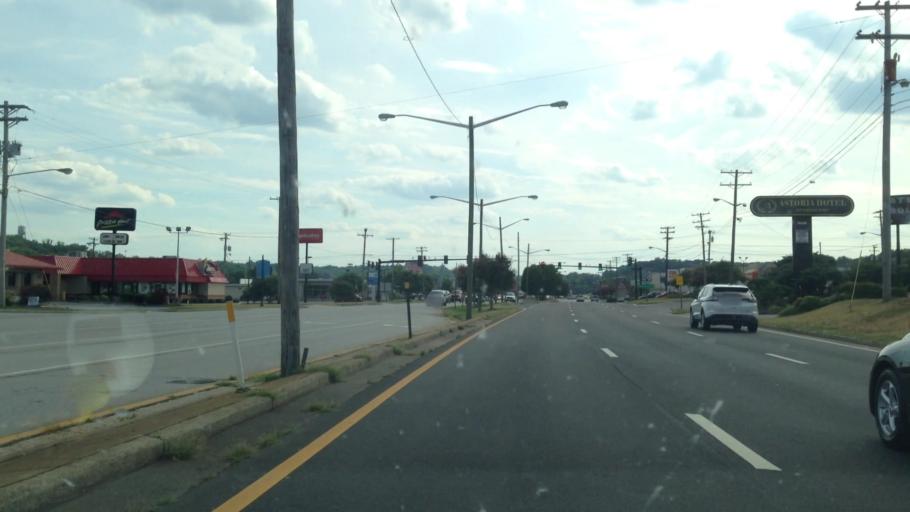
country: US
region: Virginia
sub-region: City of Danville
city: Danville
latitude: 36.5870
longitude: -79.4227
